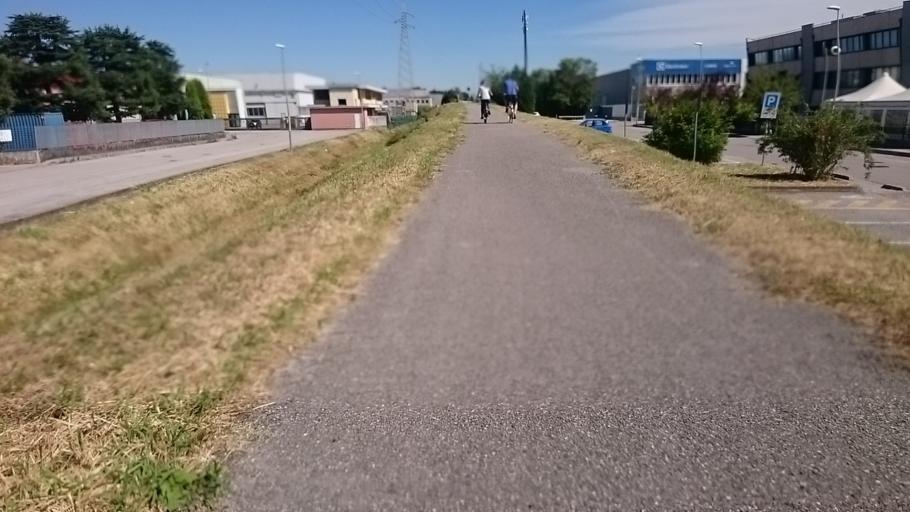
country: IT
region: Veneto
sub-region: Provincia di Padova
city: Noventa
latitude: 45.4043
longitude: 11.9370
